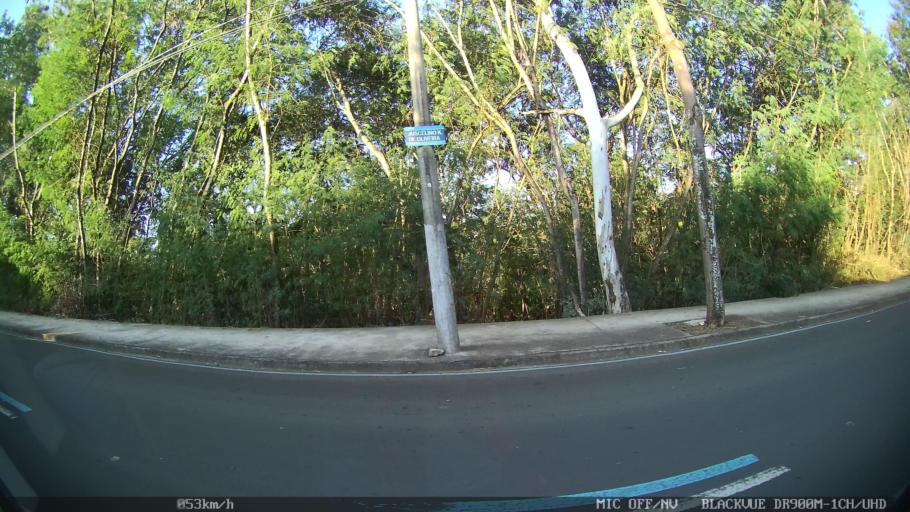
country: BR
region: Sao Paulo
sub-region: Piracicaba
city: Piracicaba
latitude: -22.7107
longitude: -47.6527
